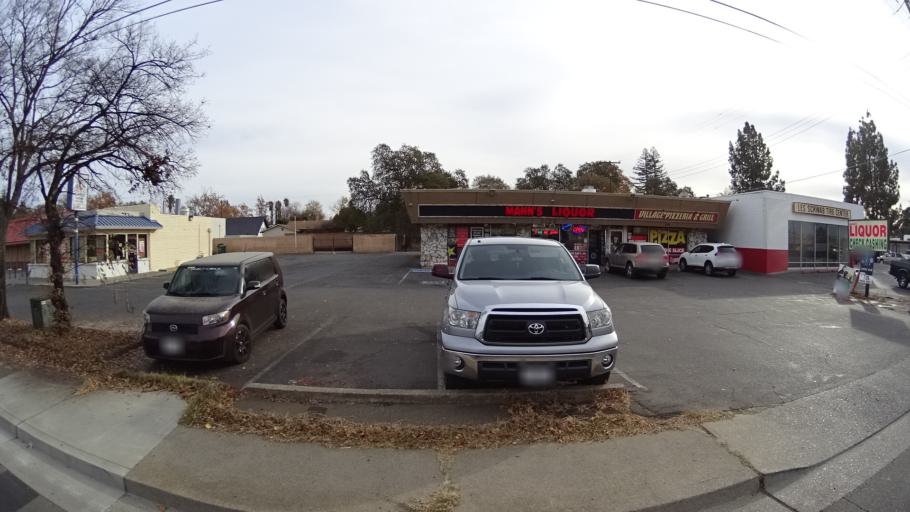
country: US
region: California
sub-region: Sacramento County
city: Citrus Heights
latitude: 38.7139
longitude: -121.2903
